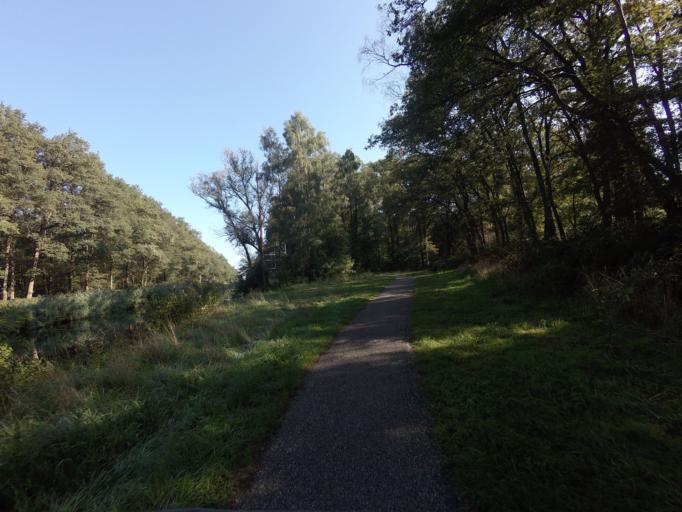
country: NL
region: Overijssel
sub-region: Gemeente Raalte
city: Raalte
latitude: 52.3428
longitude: 6.2717
